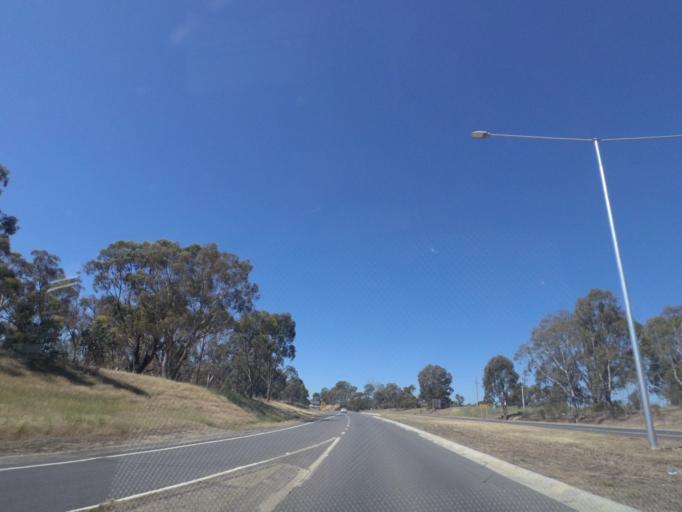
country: AU
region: Victoria
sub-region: Murrindindi
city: Kinglake West
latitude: -37.0305
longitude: 145.1028
